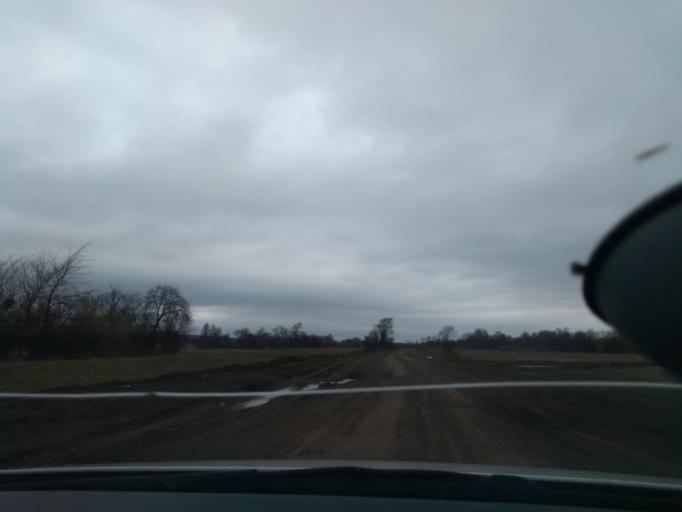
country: RU
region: Perm
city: Orda
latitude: 57.2350
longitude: 56.6106
